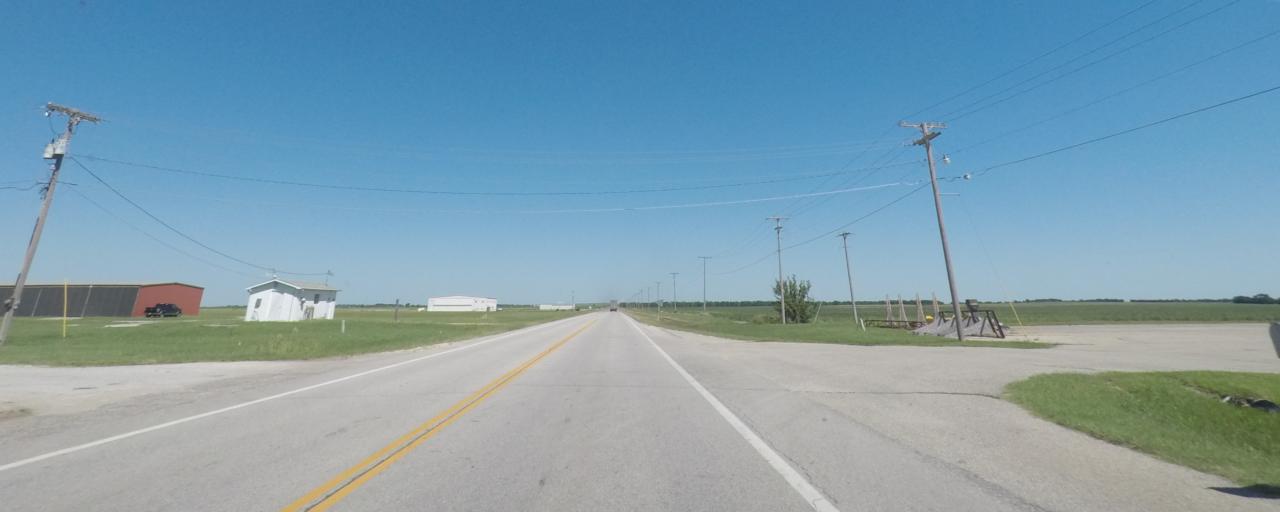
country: US
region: Kansas
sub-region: Sumner County
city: Wellington
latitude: 37.3251
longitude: -97.3849
